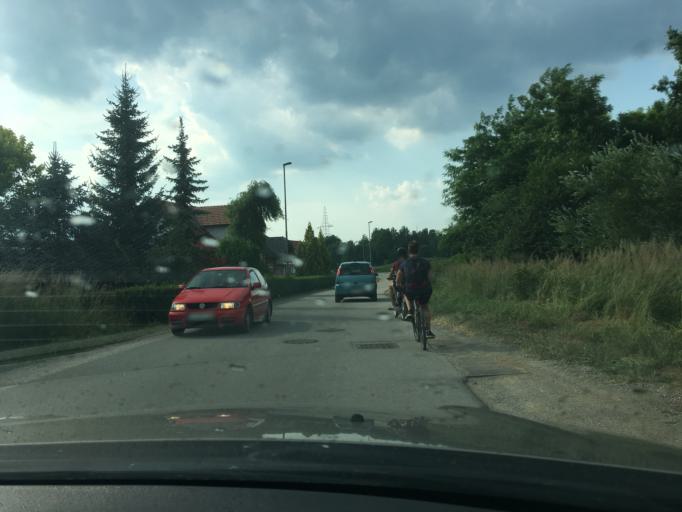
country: SI
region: Kocevje
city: Kocevje
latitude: 45.6460
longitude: 14.8678
